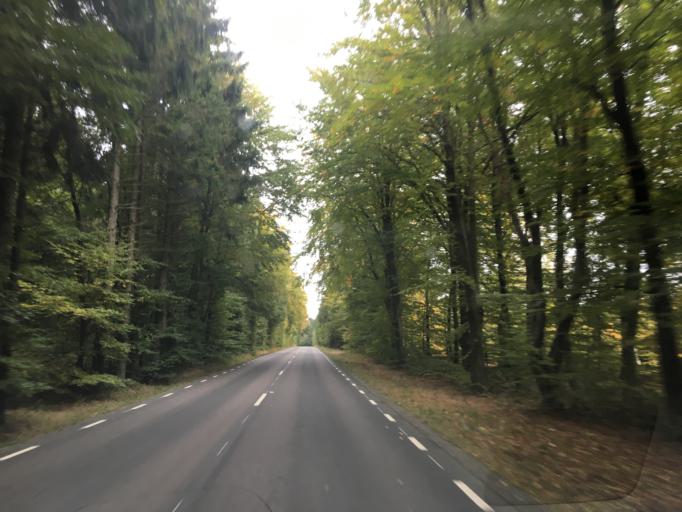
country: SE
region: Skane
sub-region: Simrishamns Kommun
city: Kivik
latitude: 55.6331
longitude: 14.0993
